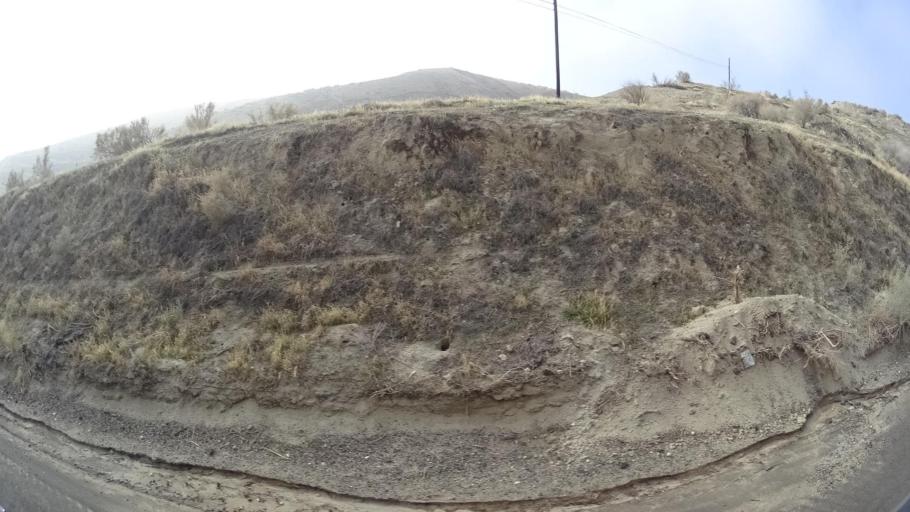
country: US
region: California
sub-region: Kern County
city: Ford City
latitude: 35.1666
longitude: -119.4053
